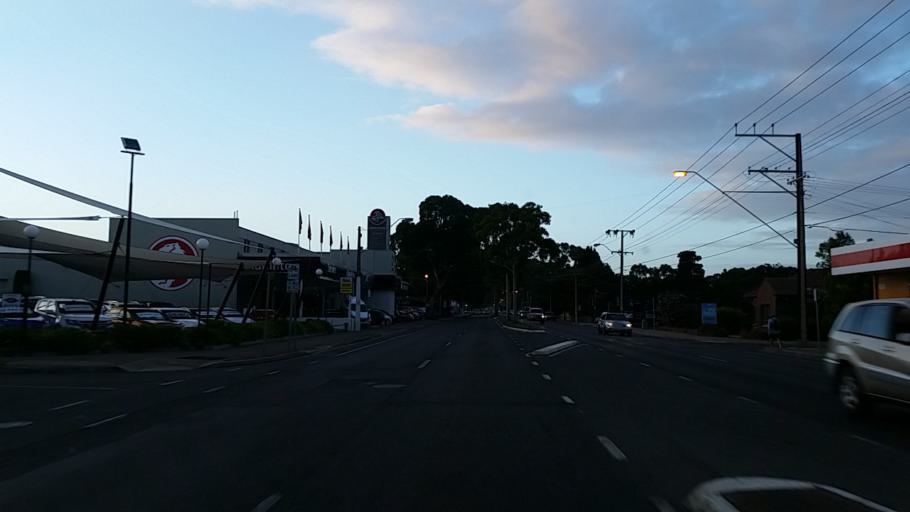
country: AU
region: South Australia
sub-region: Holdfast Bay
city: North Brighton
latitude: -35.0010
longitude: 138.5218
